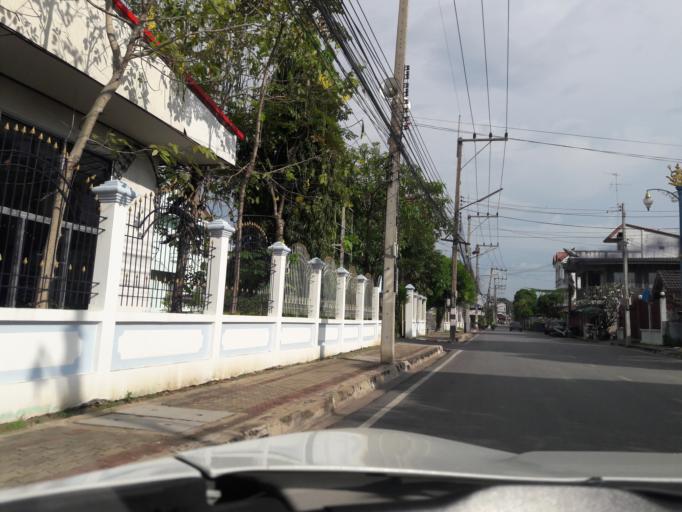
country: TH
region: Lop Buri
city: Ban Mi
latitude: 15.0441
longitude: 100.5371
